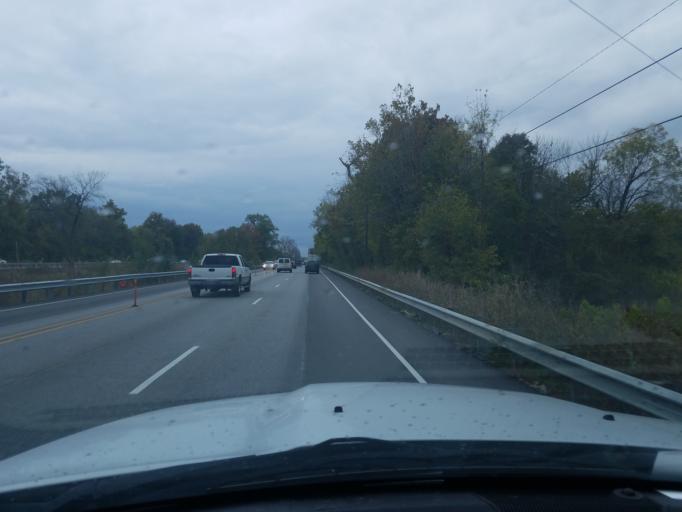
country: US
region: Kentucky
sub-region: Henderson County
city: Henderson
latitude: 37.8911
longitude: -87.5558
